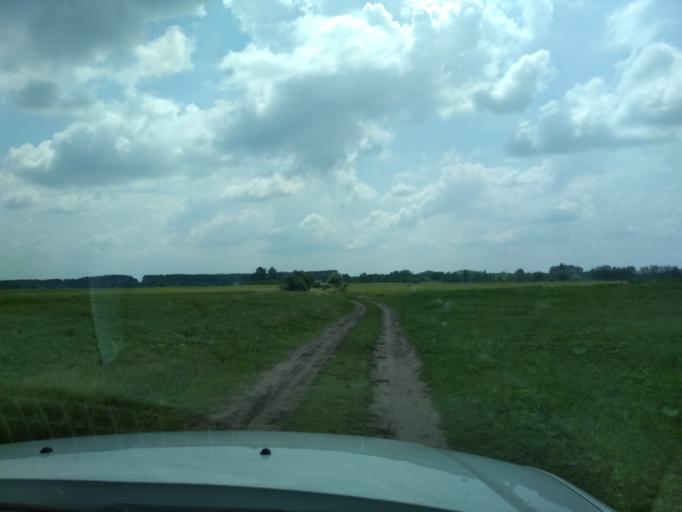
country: HU
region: Pest
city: Tapioszentmarton
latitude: 47.3729
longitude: 19.7509
